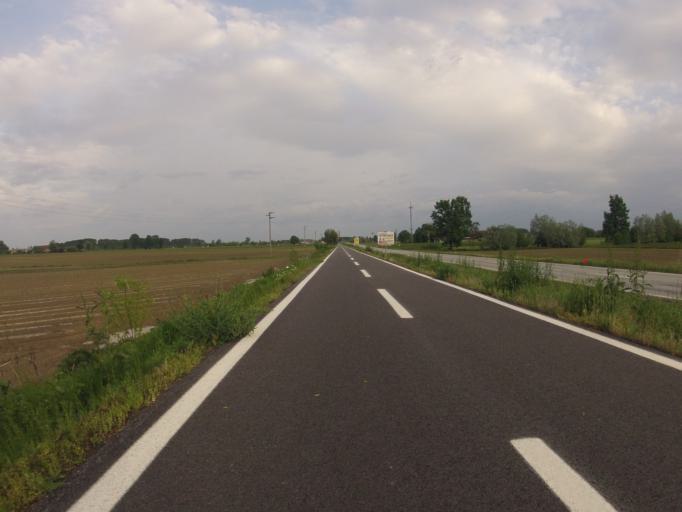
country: IT
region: Piedmont
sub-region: Provincia di Torino
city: Villafranca Piemonte
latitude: 44.7767
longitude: 7.5170
